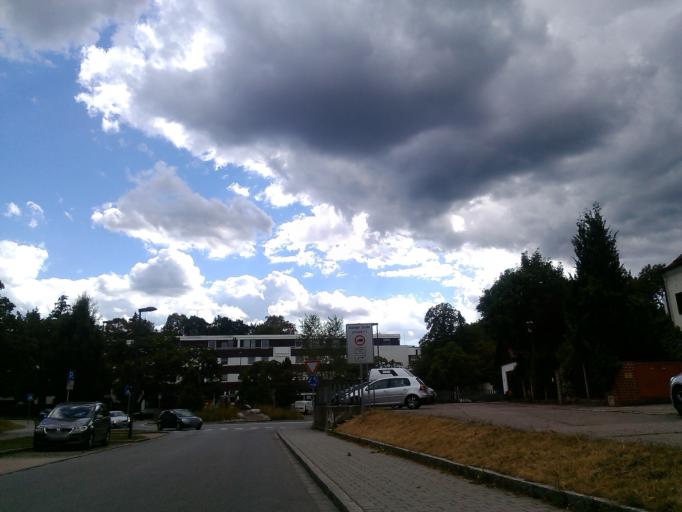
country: DE
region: Bavaria
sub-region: Upper Bavaria
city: Grafelfing
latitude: 48.1296
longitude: 11.4329
